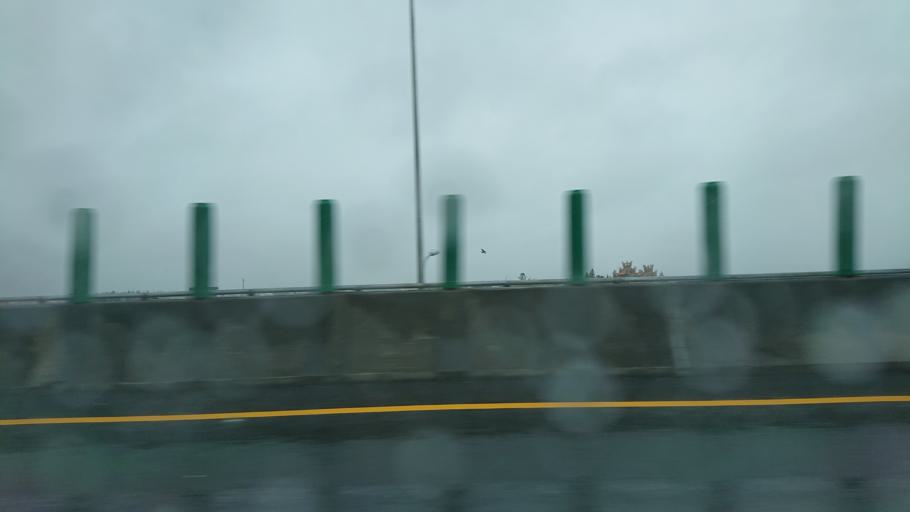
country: TW
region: Taiwan
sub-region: Chiayi
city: Taibao
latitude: 23.6411
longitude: 120.1714
